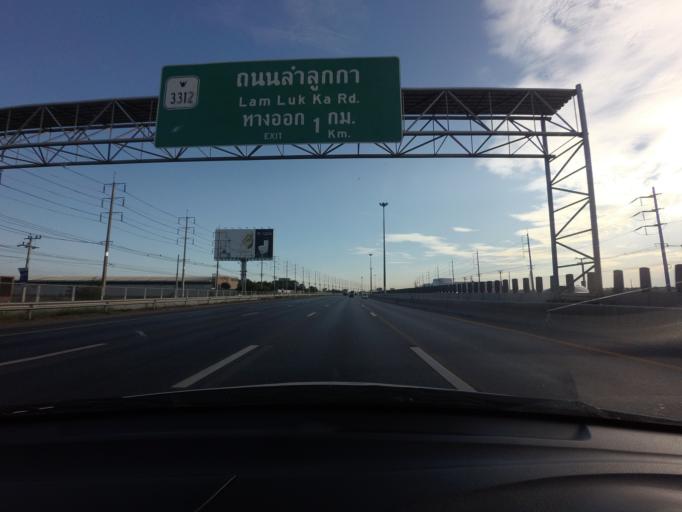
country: TH
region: Pathum Thani
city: Lam Luk Ka
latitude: 13.9521
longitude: 100.7128
